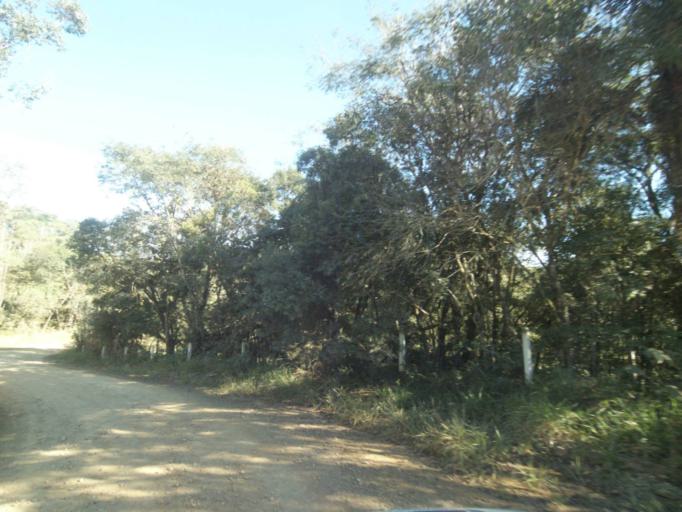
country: BR
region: Parana
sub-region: Tibagi
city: Tibagi
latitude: -24.5509
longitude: -50.5182
